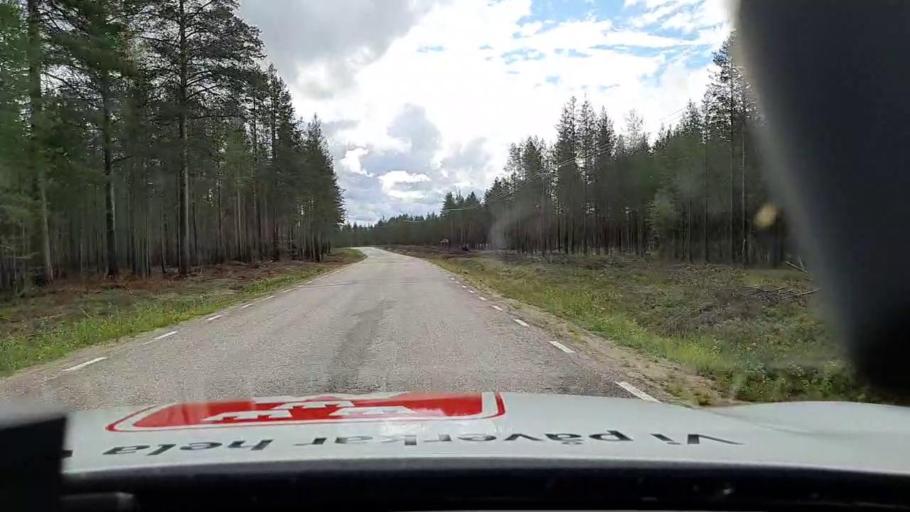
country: SE
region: Norrbotten
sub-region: Overkalix Kommun
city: OEverkalix
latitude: 66.2518
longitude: 22.8756
